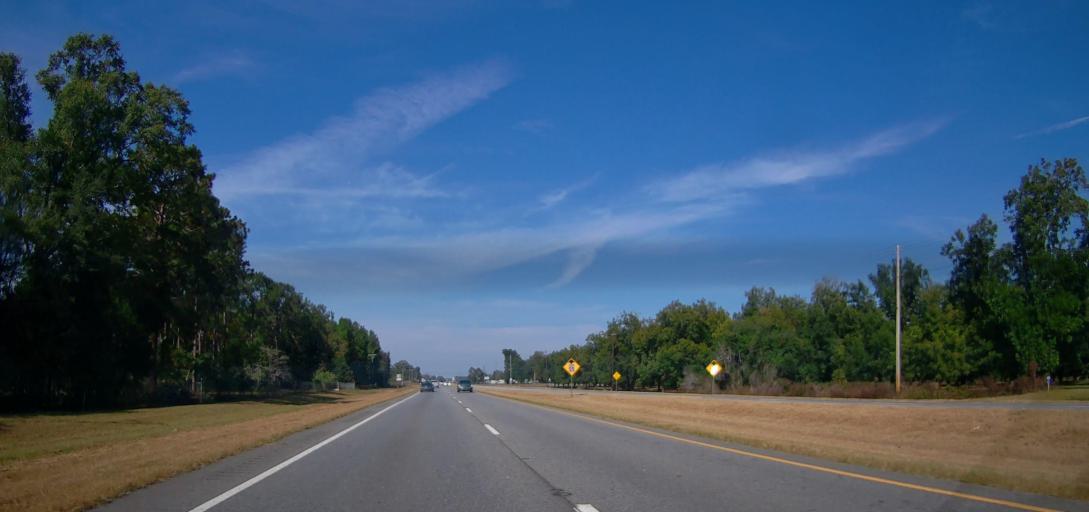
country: US
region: Georgia
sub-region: Dougherty County
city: Putney
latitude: 31.5136
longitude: -84.1156
